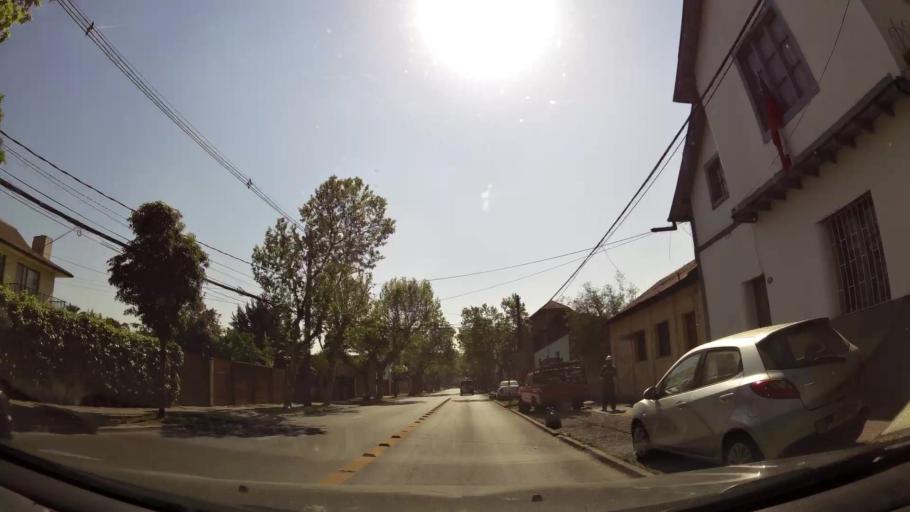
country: CL
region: Santiago Metropolitan
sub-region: Provincia de Maipo
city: San Bernardo
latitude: -33.5876
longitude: -70.7006
